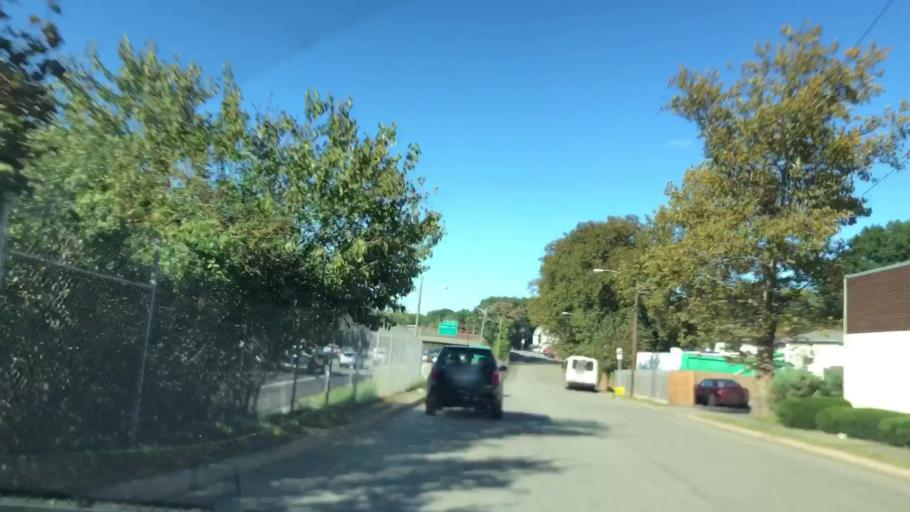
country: US
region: New Jersey
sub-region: Essex County
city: Bloomfield
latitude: 40.7931
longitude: -74.1920
